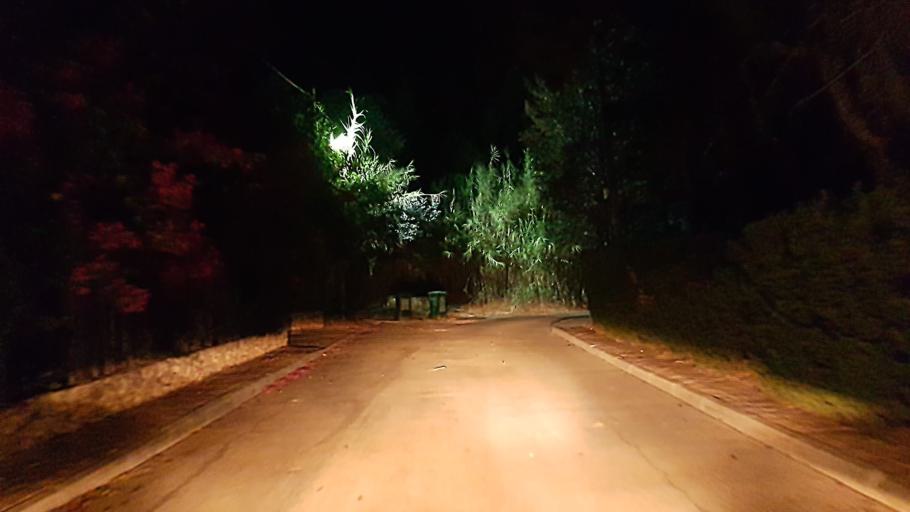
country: IL
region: Central District
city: Hod HaSharon
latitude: 32.1486
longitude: 34.8996
